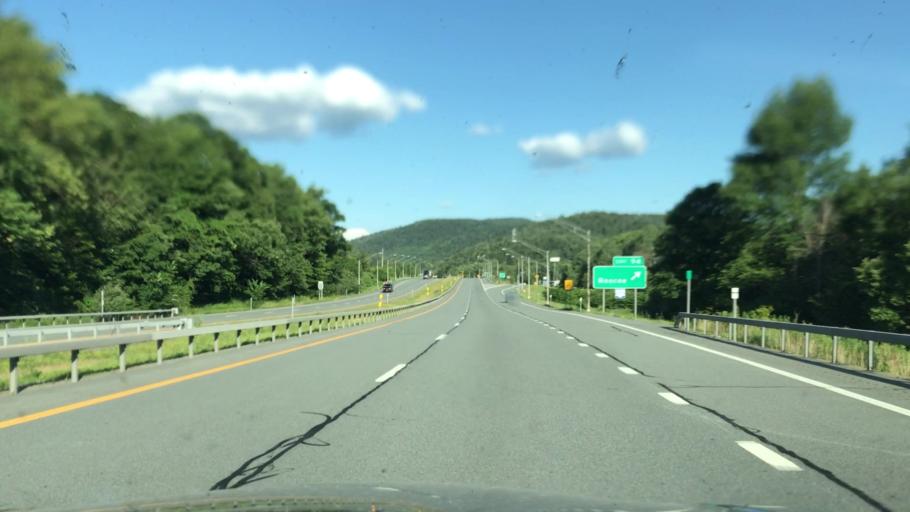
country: US
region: New York
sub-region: Sullivan County
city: Livingston Manor
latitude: 41.9334
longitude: -74.9191
